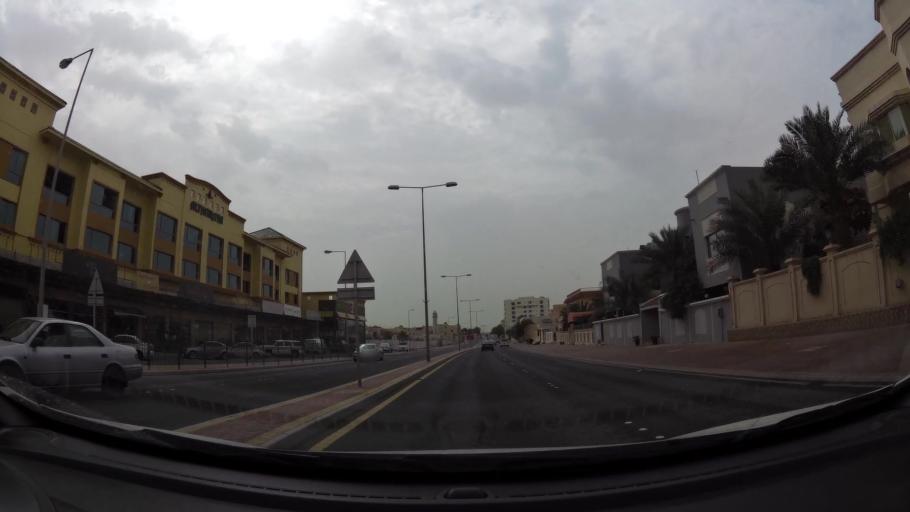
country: BH
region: Northern
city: Ar Rifa'
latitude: 26.1348
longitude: 50.5503
